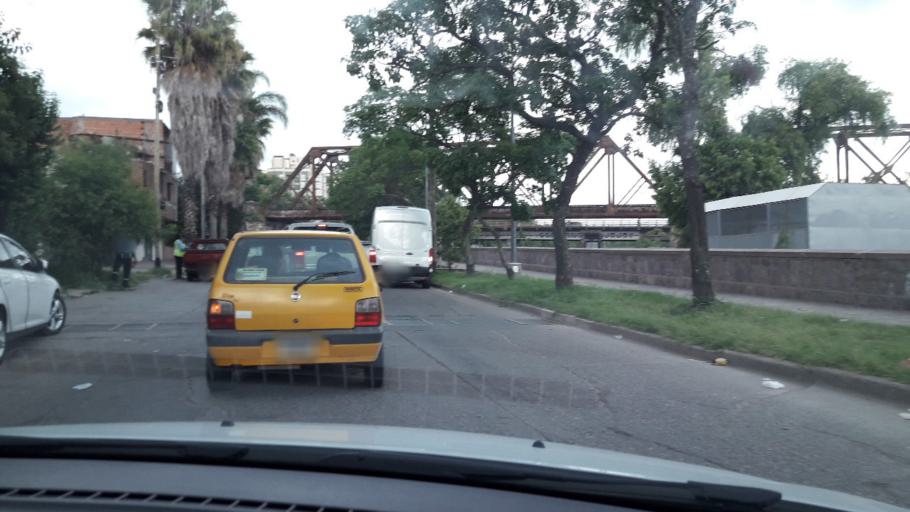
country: AR
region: Jujuy
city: San Salvador de Jujuy
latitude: -24.1907
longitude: -65.2918
